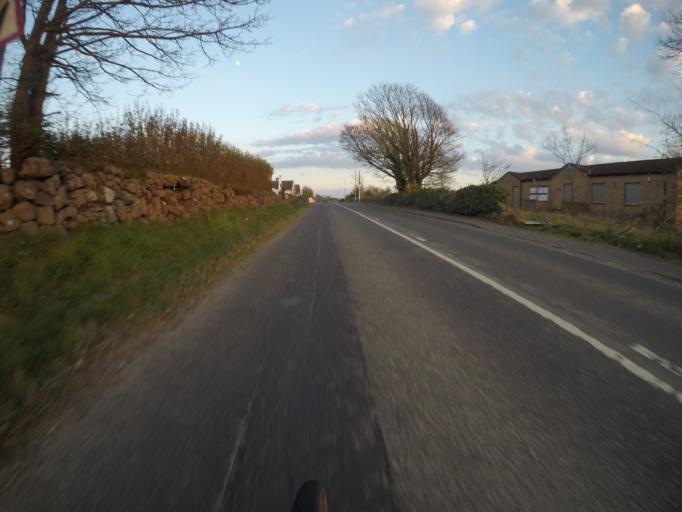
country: GB
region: Scotland
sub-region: South Ayrshire
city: Troon
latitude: 55.5599
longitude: -4.6308
